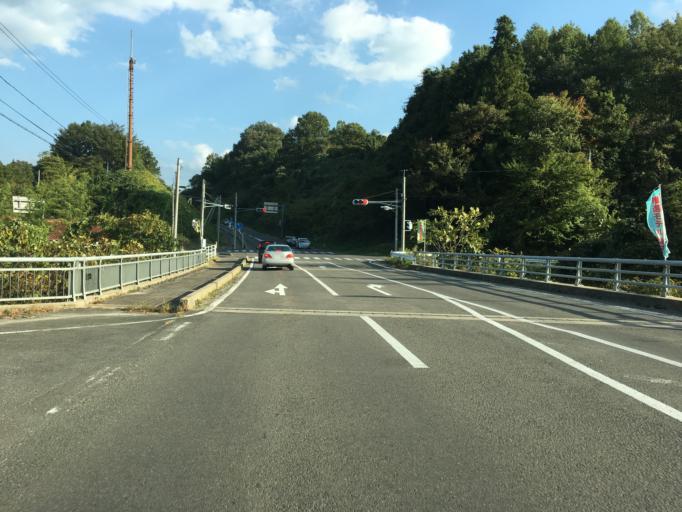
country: JP
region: Fukushima
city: Fukushima-shi
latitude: 37.6719
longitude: 140.5138
